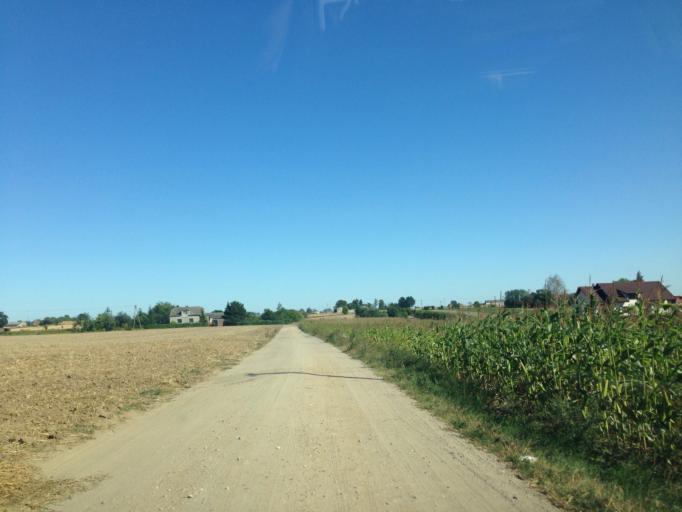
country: PL
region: Kujawsko-Pomorskie
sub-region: Powiat brodnicki
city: Brodnica
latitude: 53.2150
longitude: 19.3853
